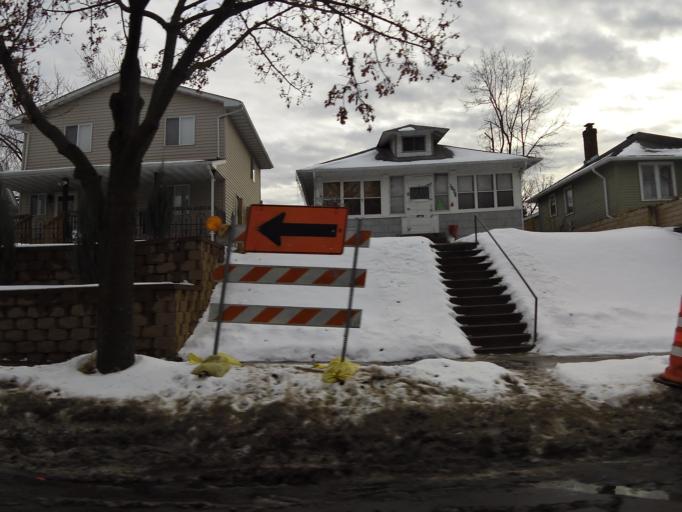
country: US
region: Minnesota
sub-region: Ramsey County
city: Maplewood
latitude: 44.9667
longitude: -93.0293
